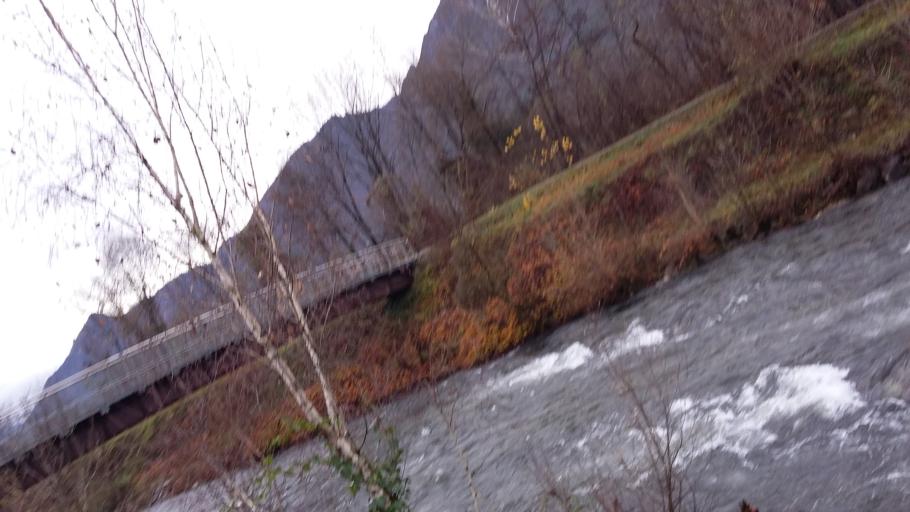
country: IT
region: Lombardy
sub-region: Provincia di Brescia
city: Ponte Caffaro
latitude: 45.8206
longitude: 10.5336
